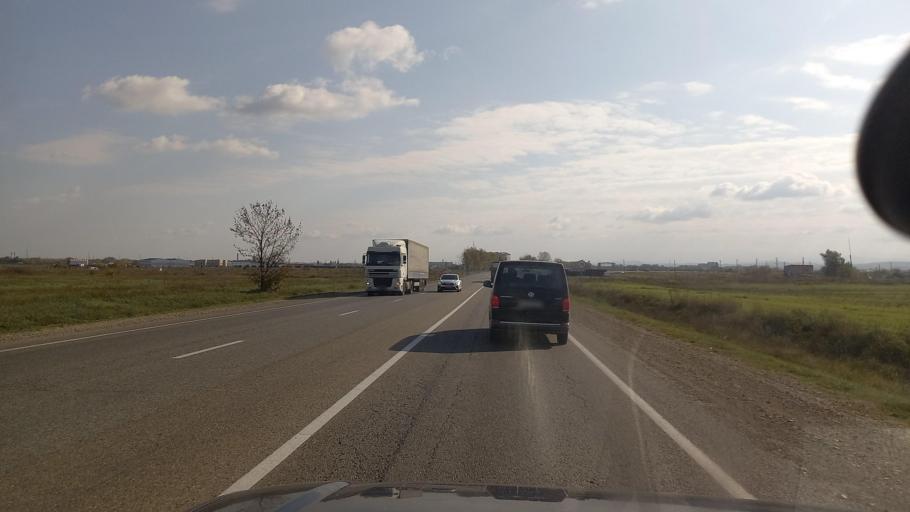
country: RU
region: Krasnodarskiy
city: Abinsk
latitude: 44.8729
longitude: 38.1198
